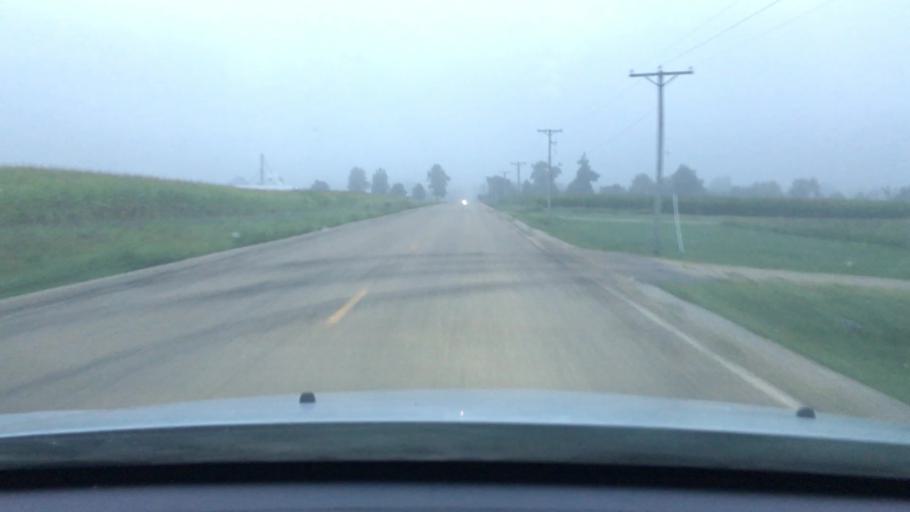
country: US
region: Illinois
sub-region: DeKalb County
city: Waterman
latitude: 41.7841
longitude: -88.7739
